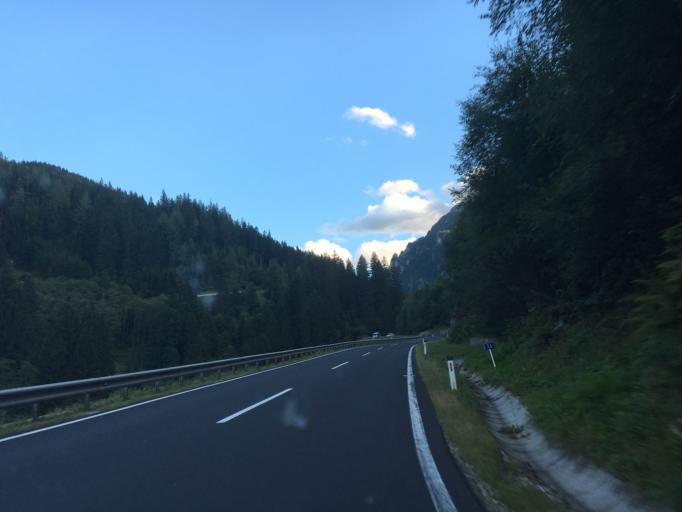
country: AT
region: Styria
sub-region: Politischer Bezirk Liezen
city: Trieben
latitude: 47.4711
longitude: 14.4851
